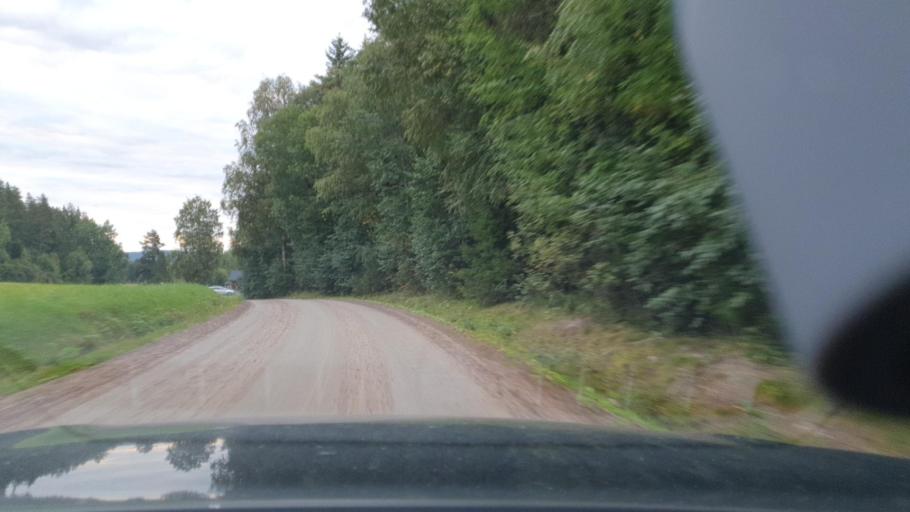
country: SE
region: Vaermland
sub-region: Munkfors Kommun
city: Munkfors
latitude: 59.8299
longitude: 13.5052
